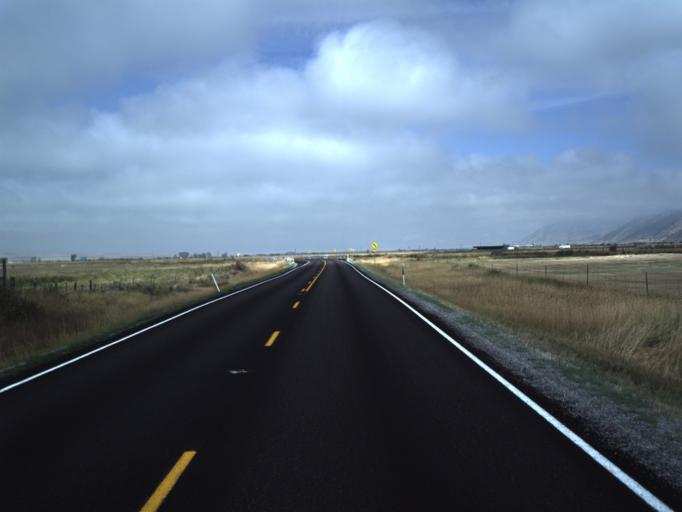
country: US
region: Utah
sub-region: Rich County
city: Randolph
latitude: 41.5003
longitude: -111.1229
